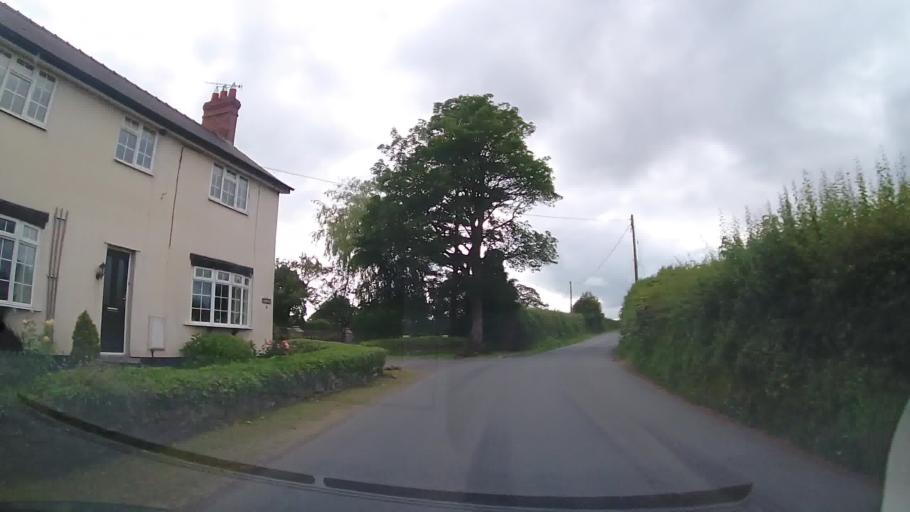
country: GB
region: England
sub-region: Shropshire
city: Wem
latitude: 52.9029
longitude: -2.7159
